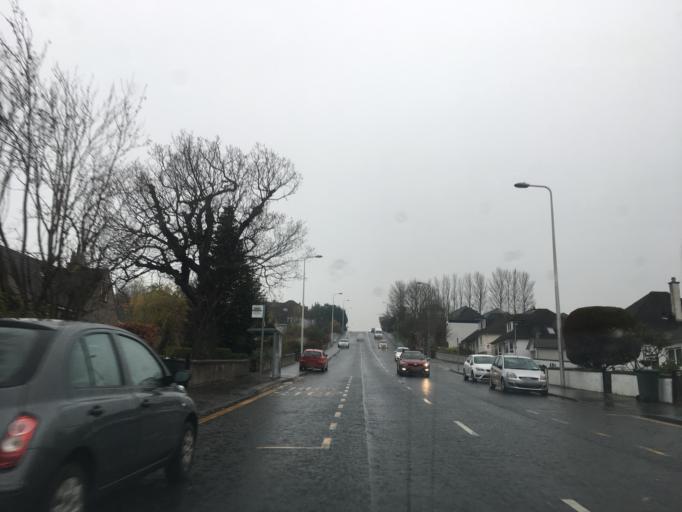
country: GB
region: Scotland
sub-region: Edinburgh
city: Currie
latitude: 55.9576
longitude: -3.2996
